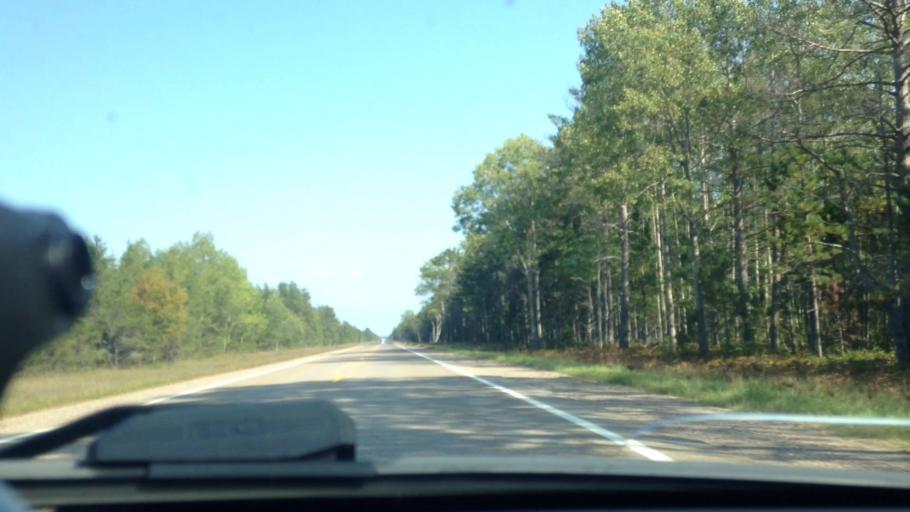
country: US
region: Michigan
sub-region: Mackinac County
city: Saint Ignace
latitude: 46.3585
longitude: -84.8573
